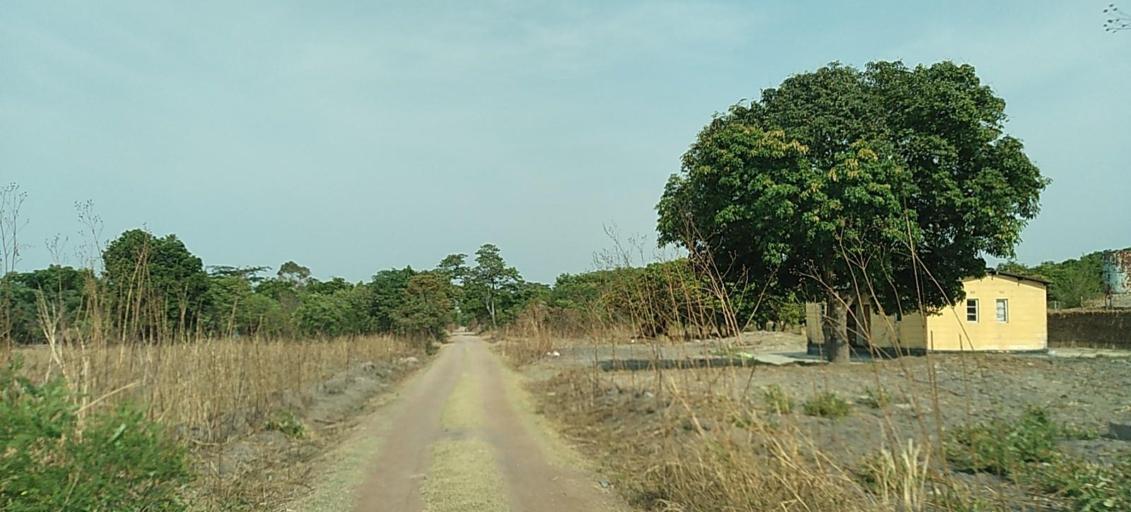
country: ZM
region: Copperbelt
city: Ndola
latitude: -13.2219
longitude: 28.6693
